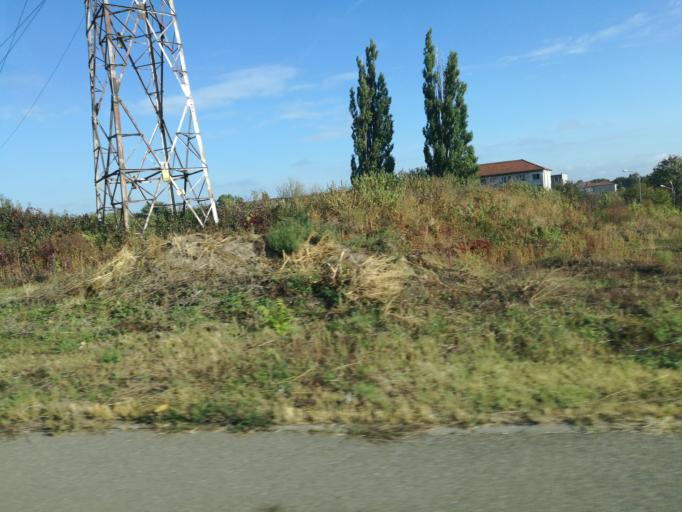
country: RO
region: Bihor
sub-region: Comuna Biharea
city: Oradea
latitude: 47.0400
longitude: 21.9308
